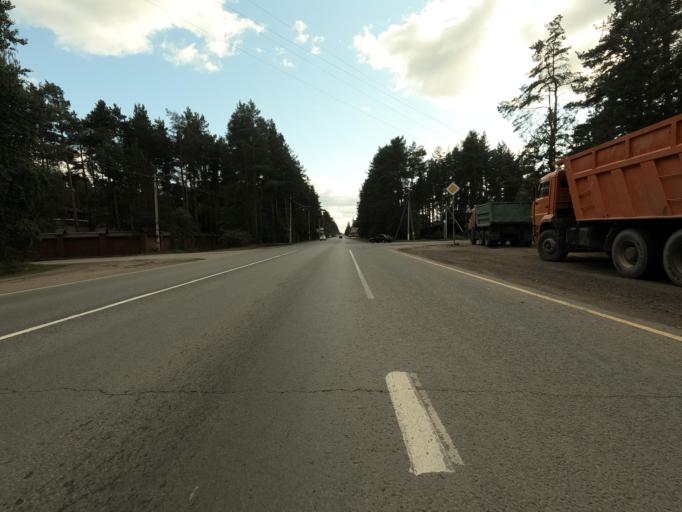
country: RU
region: Leningrad
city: Vsevolozhsk
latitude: 60.0022
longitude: 30.6625
